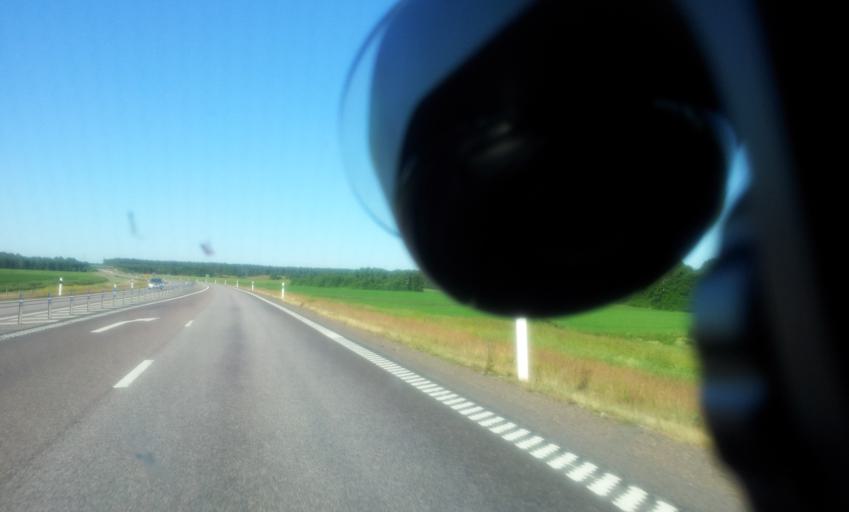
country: SE
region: Kalmar
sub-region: Kalmar Kommun
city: Ljungbyholm
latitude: 56.6126
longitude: 16.1422
